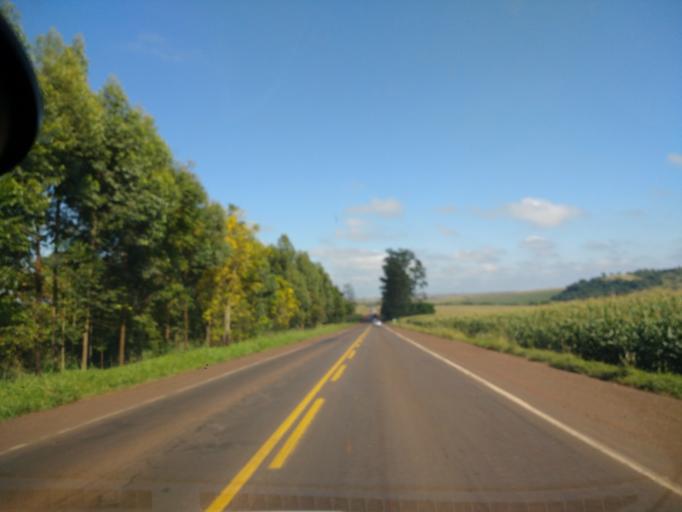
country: BR
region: Parana
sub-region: Paicandu
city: Paicandu
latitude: -23.5090
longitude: -52.1707
